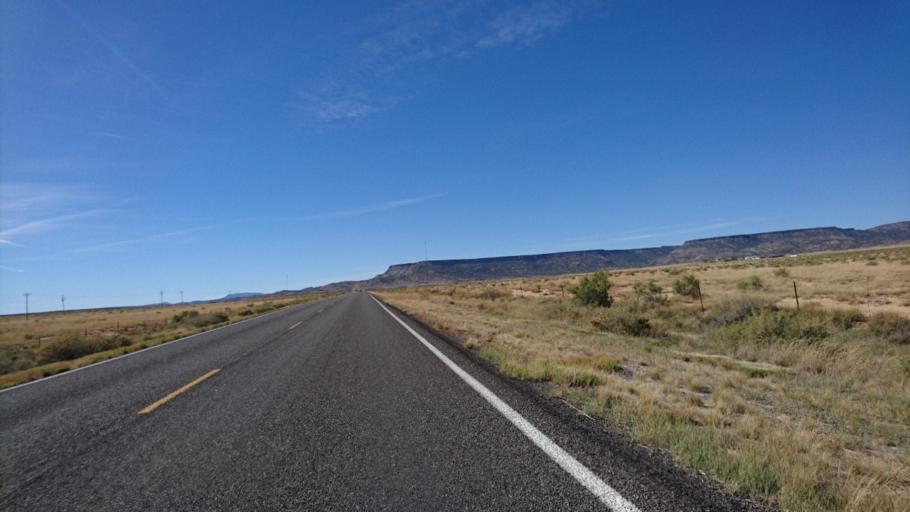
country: US
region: New Mexico
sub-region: Cibola County
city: Skyline-Ganipa
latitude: 35.0824
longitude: -107.6196
